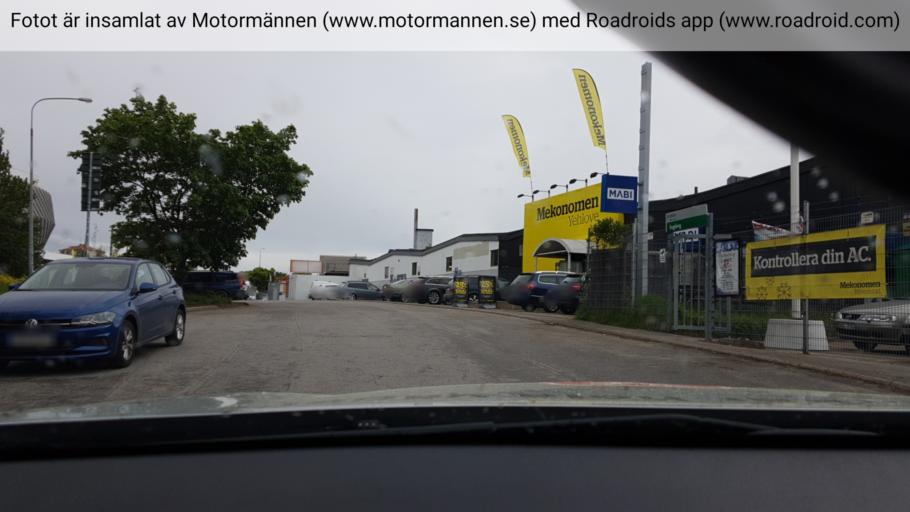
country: SE
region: Stockholm
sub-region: Stockholms Kommun
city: Arsta
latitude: 59.2881
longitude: 18.0829
